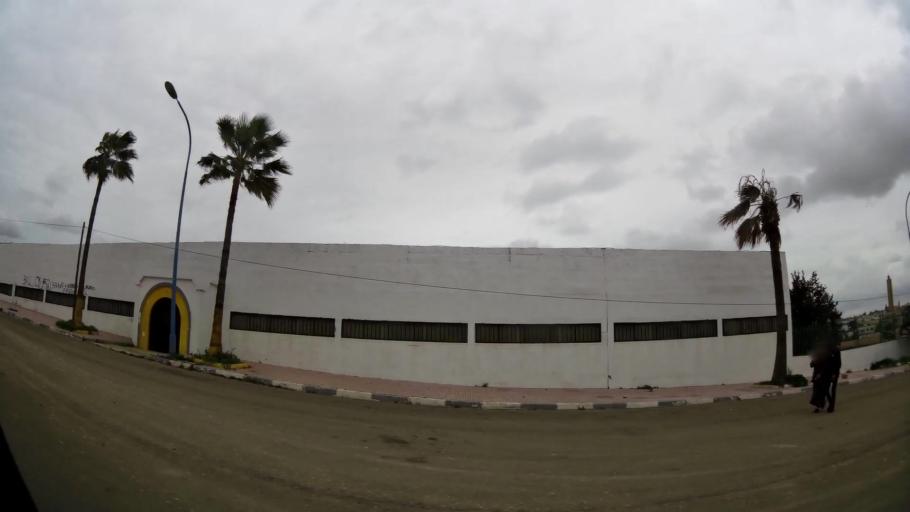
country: MA
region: Grand Casablanca
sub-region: Mediouna
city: Tit Mellil
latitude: 33.5670
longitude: -7.5382
